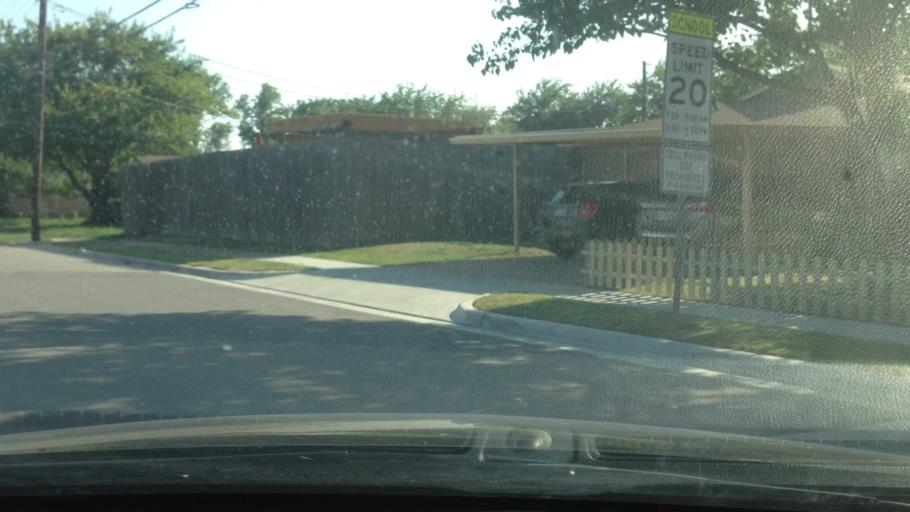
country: US
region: Texas
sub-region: Tarrant County
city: Watauga
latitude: 32.8637
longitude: -97.2500
